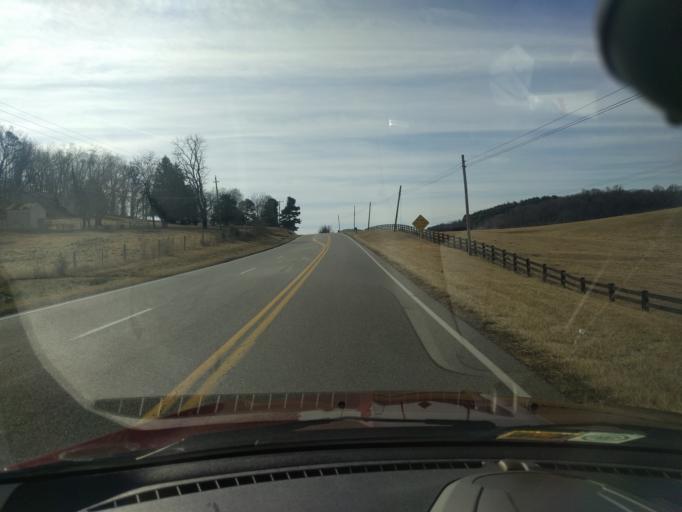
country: US
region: Virginia
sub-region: Augusta County
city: Weyers Cave
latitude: 38.2699
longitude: -78.9513
